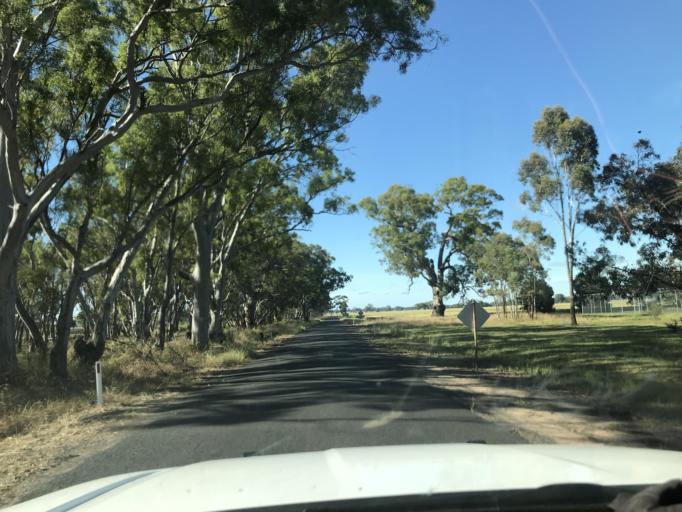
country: AU
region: Victoria
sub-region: Horsham
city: Horsham
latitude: -37.0343
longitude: 141.7300
